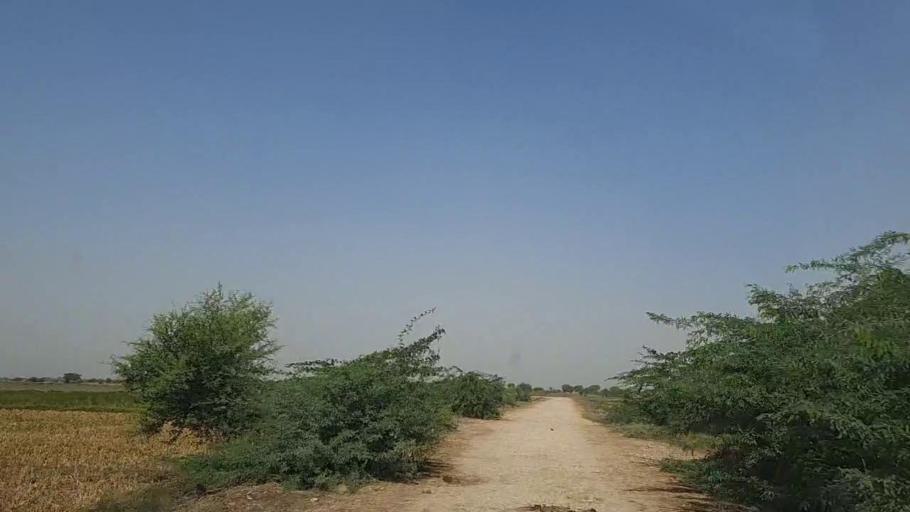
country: PK
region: Sindh
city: Daro Mehar
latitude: 24.7507
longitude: 68.1398
